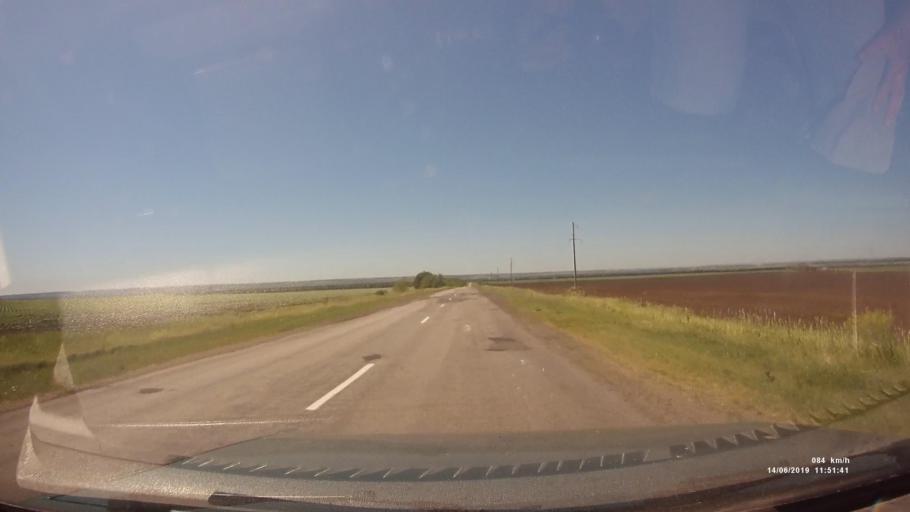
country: RU
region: Rostov
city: Kazanskaya
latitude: 49.8413
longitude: 41.2416
